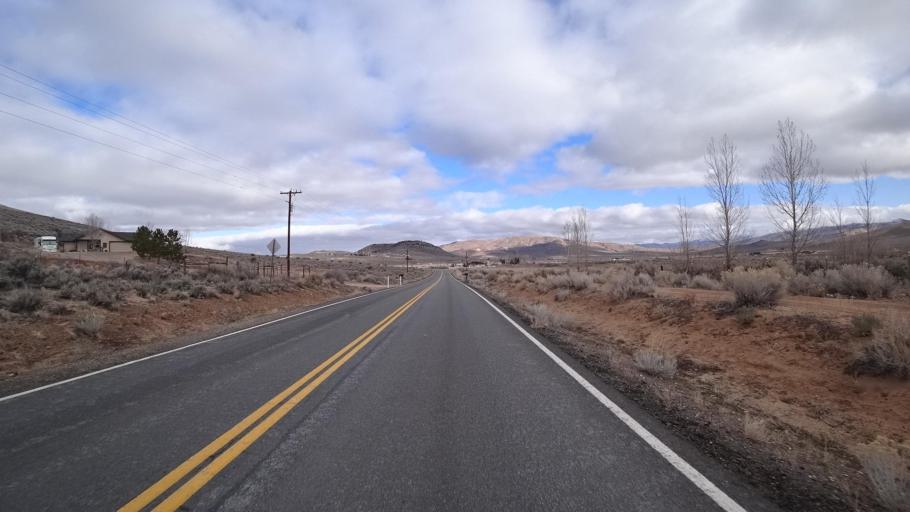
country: US
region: Nevada
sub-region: Washoe County
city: Cold Springs
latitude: 39.8579
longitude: -119.9352
